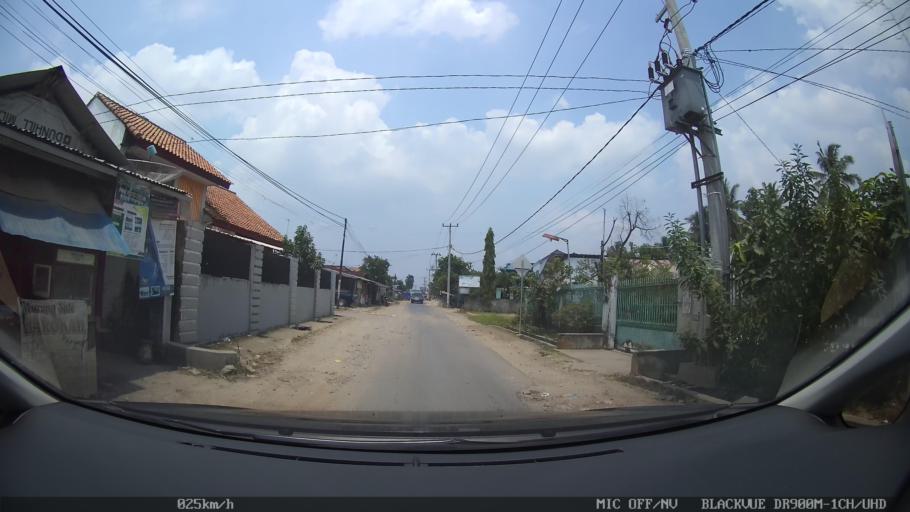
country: ID
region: Lampung
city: Pringsewu
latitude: -5.3495
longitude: 104.9812
